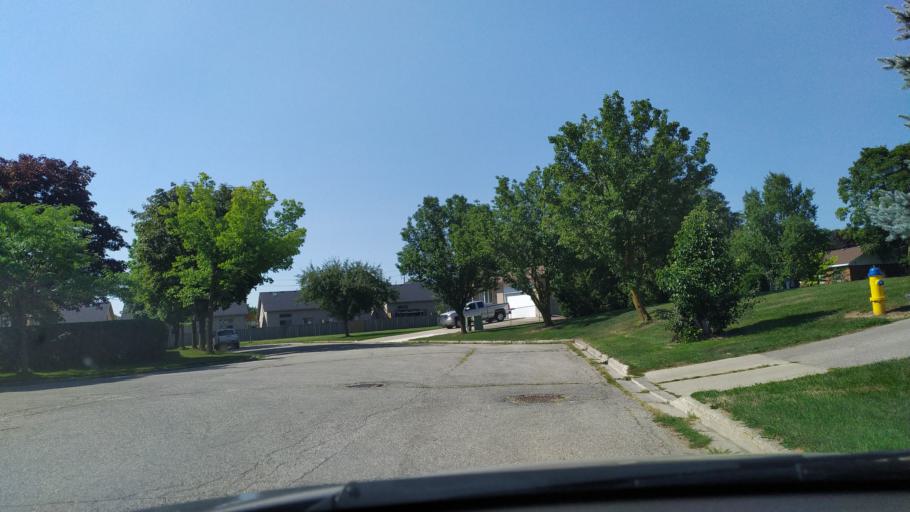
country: CA
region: Ontario
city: Stratford
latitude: 43.3853
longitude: -80.9701
